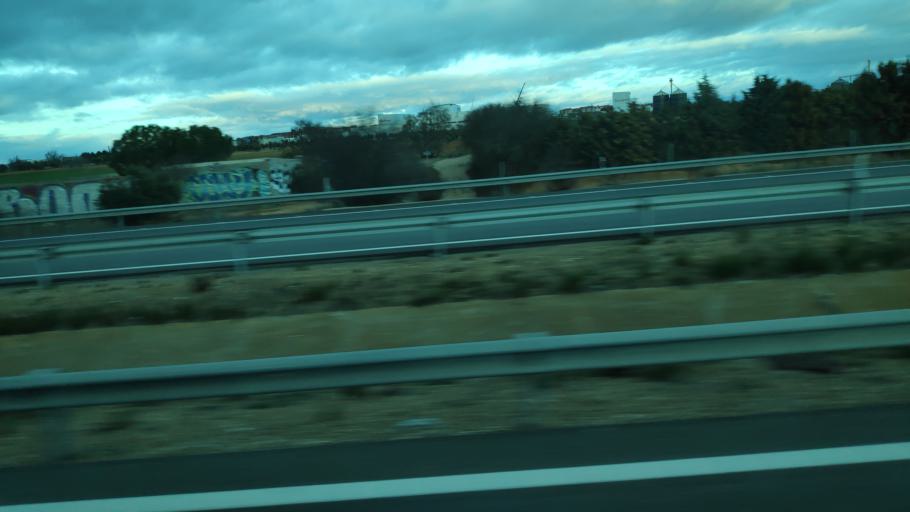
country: ES
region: Castille-La Mancha
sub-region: Provincia de Cuenca
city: Tarancon
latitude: 40.0072
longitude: -3.0286
